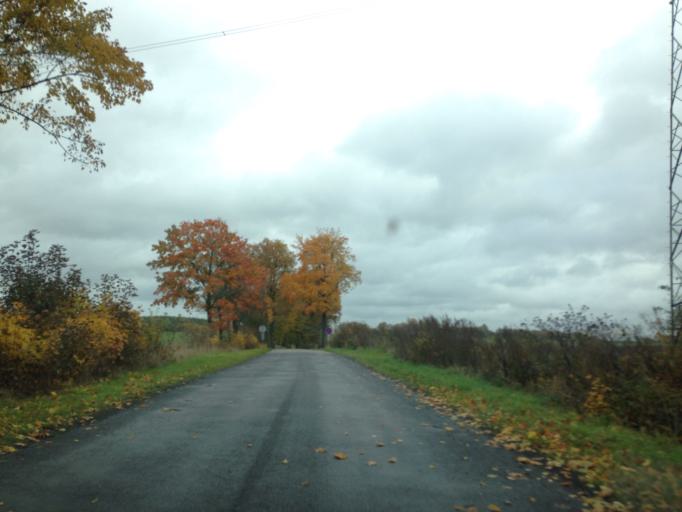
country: PL
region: Pomeranian Voivodeship
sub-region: Powiat kwidzynski
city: Ryjewo
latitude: 53.8352
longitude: 19.0216
